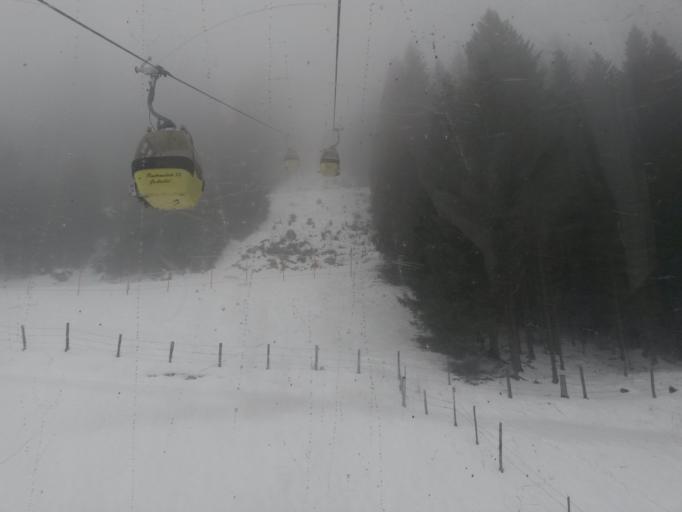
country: AT
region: Salzburg
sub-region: Politischer Bezirk Sankt Johann im Pongau
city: Dorfgastein
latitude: 47.2414
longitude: 13.1889
